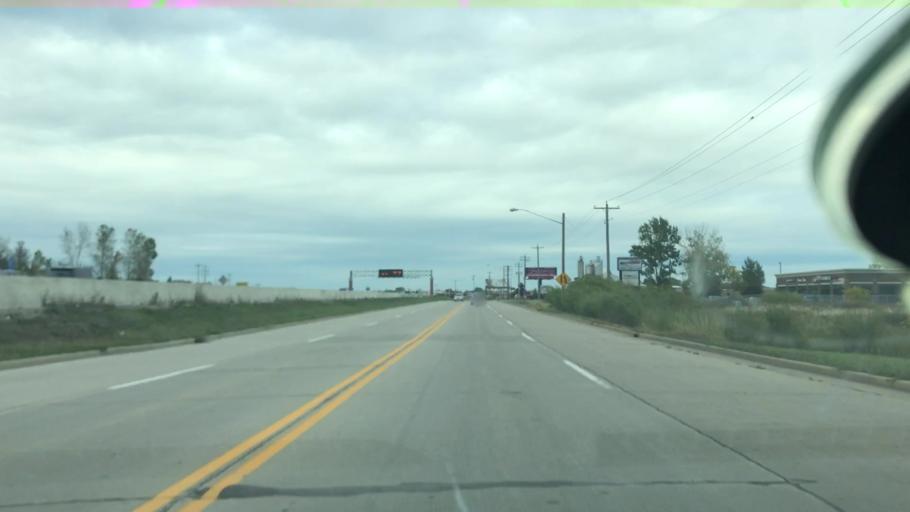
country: US
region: Wisconsin
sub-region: Brown County
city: De Pere
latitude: 44.4354
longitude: -88.1038
